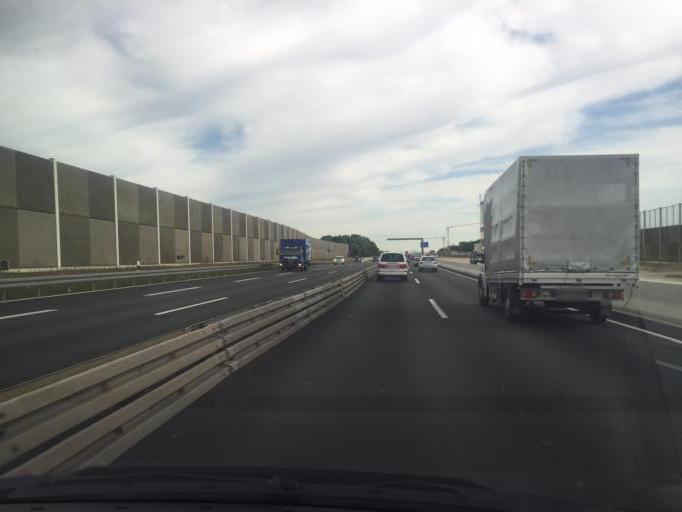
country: DE
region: North Rhine-Westphalia
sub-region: Regierungsbezirk Dusseldorf
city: Kaarst
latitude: 51.2277
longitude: 6.6385
